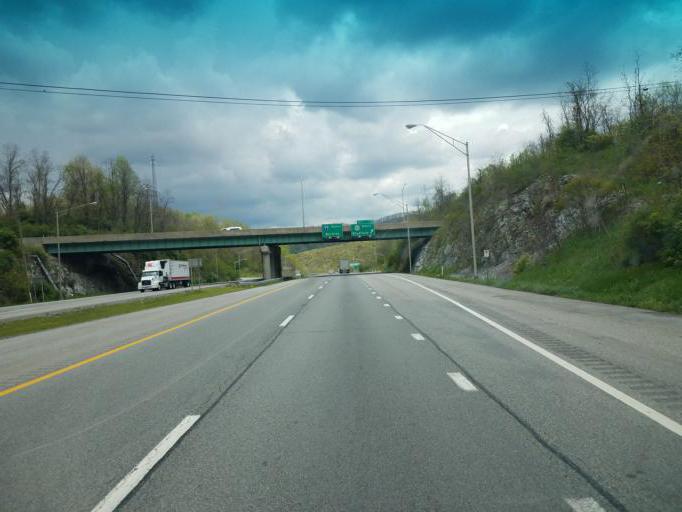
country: US
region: West Virginia
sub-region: Mercer County
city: Princeton
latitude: 37.2836
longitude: -81.1251
